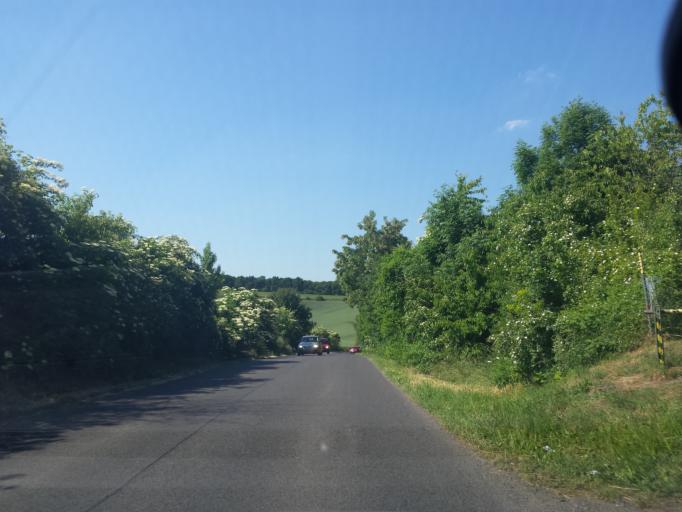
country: CZ
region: Central Bohemia
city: Nelahozeves
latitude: 50.2511
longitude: 14.2984
